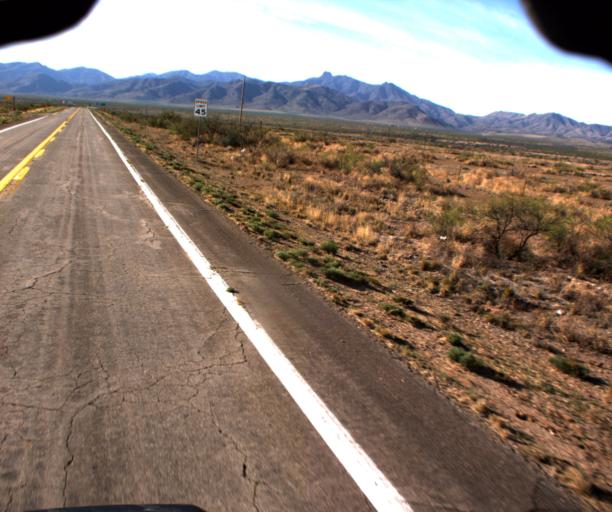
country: US
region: Arizona
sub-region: Cochise County
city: Willcox
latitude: 32.3666
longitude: -109.6233
